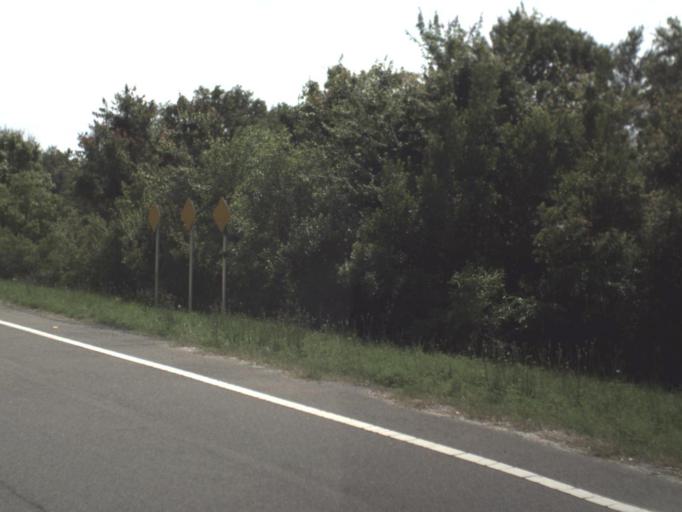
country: US
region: Florida
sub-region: Duval County
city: Jacksonville
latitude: 30.4771
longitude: -81.6294
